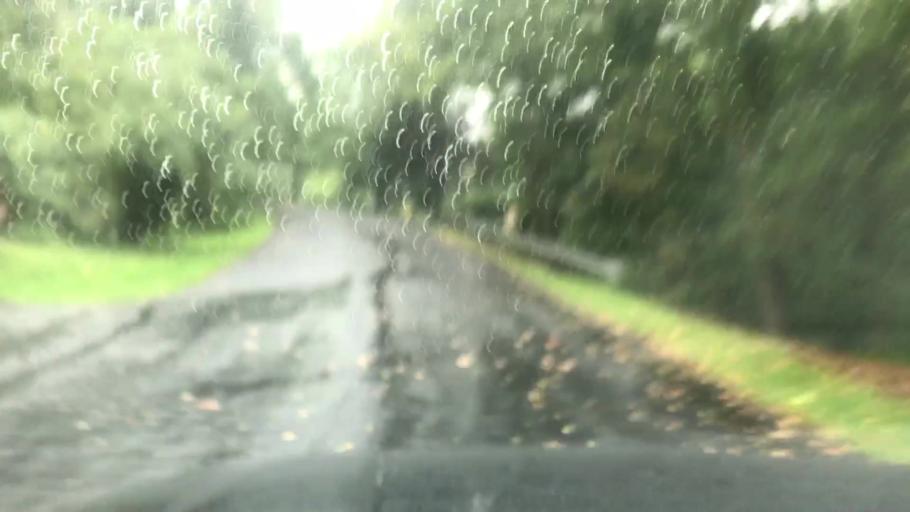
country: US
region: Pennsylvania
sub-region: Cumberland County
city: Shiremanstown
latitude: 40.1761
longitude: -76.9394
